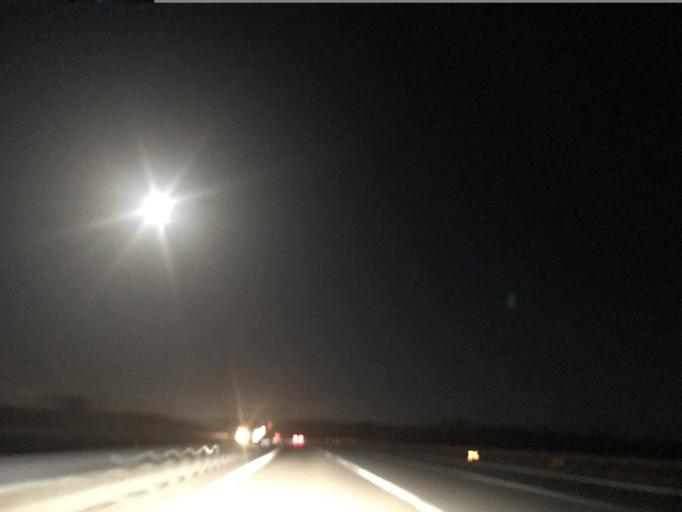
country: TR
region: Nigde
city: Ulukisla
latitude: 37.6404
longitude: 34.3839
